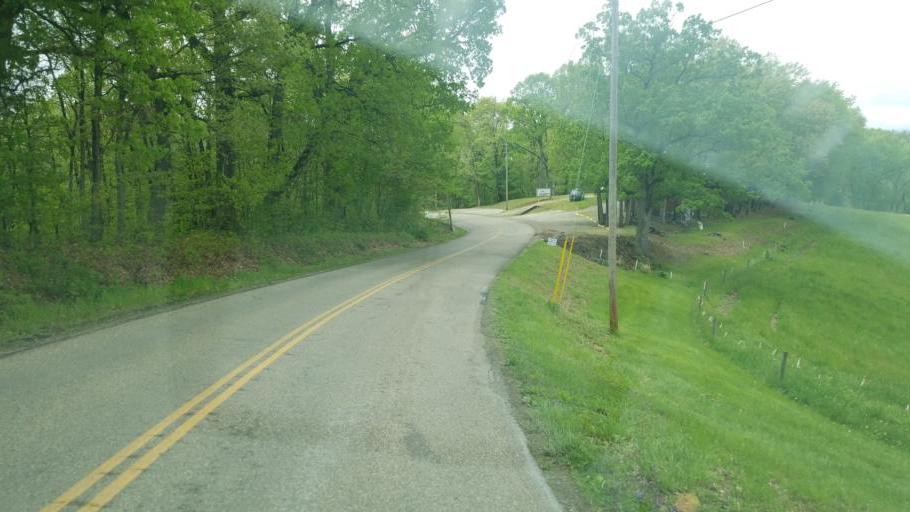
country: US
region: Ohio
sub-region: Tuscarawas County
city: Rockford
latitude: 40.4686
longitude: -81.3022
